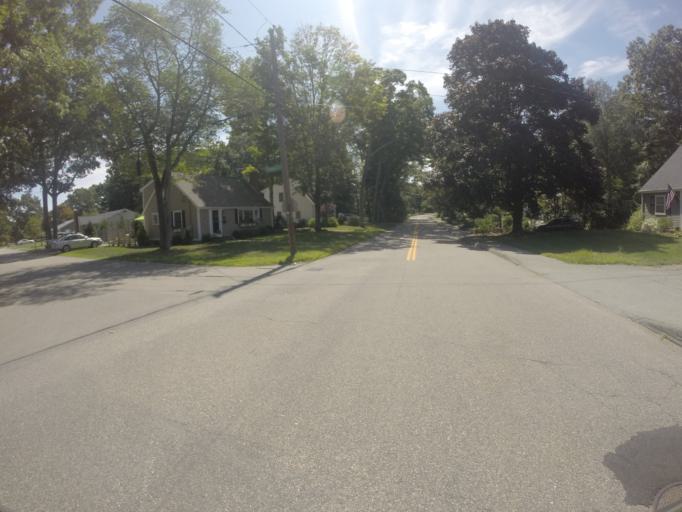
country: US
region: Massachusetts
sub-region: Bristol County
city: Easton
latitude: 42.0560
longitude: -71.1052
